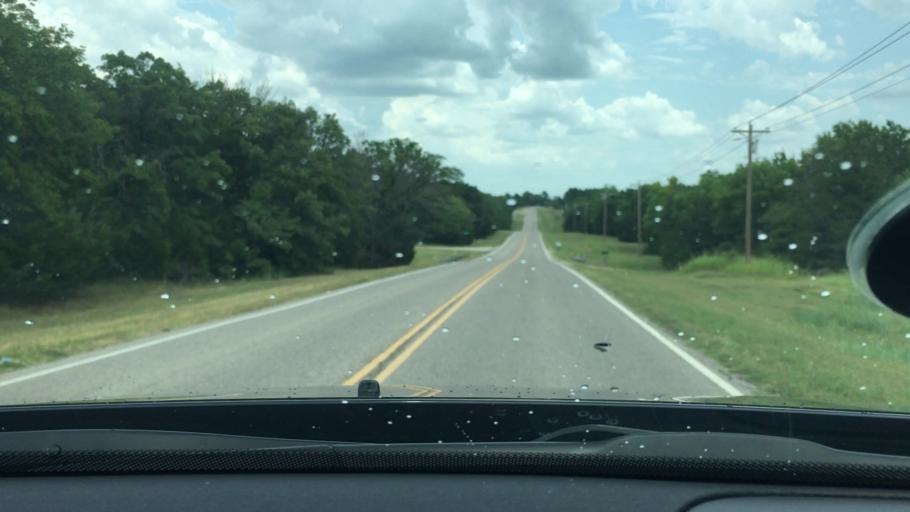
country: US
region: Oklahoma
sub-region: Love County
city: Marietta
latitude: 33.9602
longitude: -97.0272
